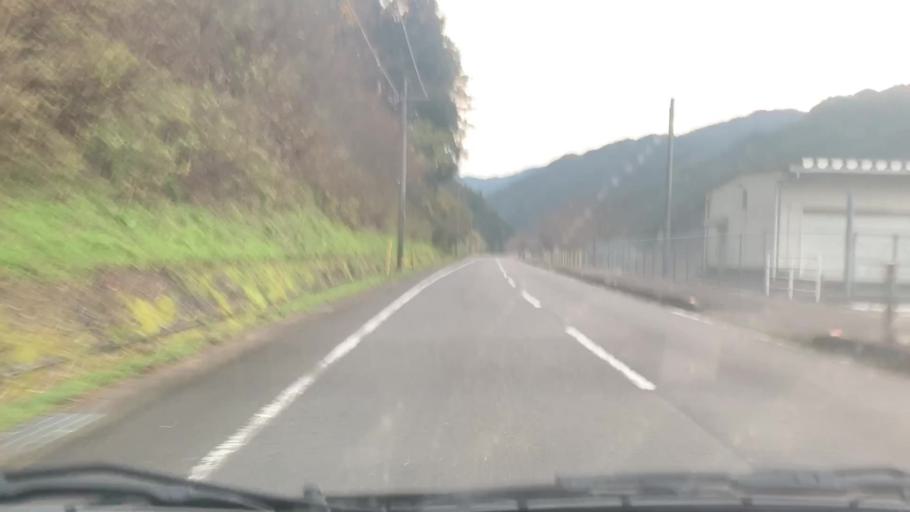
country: JP
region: Saga Prefecture
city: Kashima
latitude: 33.0348
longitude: 130.0701
